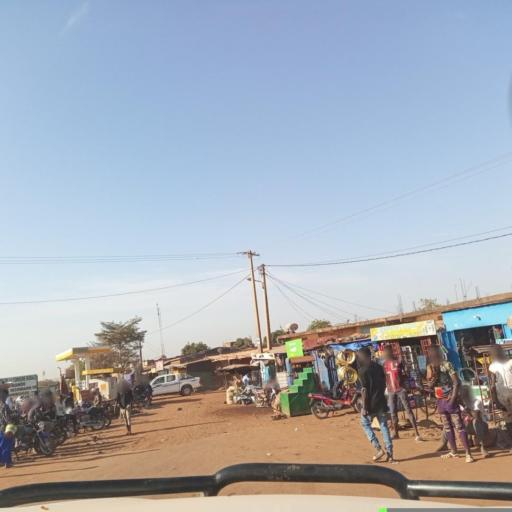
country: ML
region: Bamako
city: Bamako
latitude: 12.5603
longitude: -8.1008
